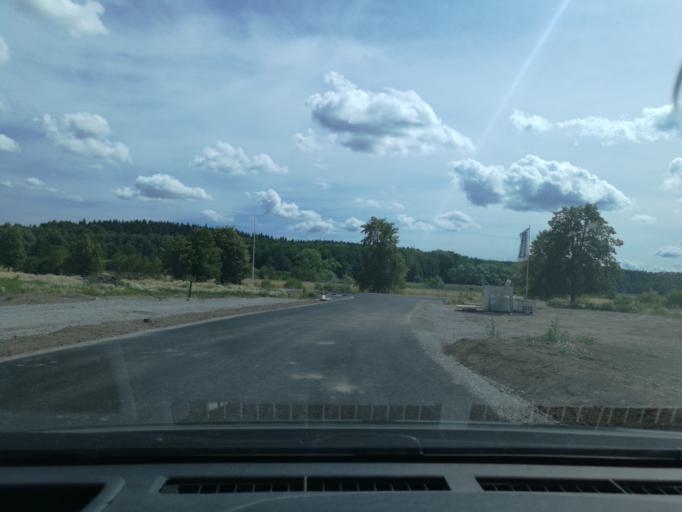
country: SE
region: Stockholm
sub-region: Sigtuna Kommun
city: Marsta
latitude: 59.6046
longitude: 17.8107
